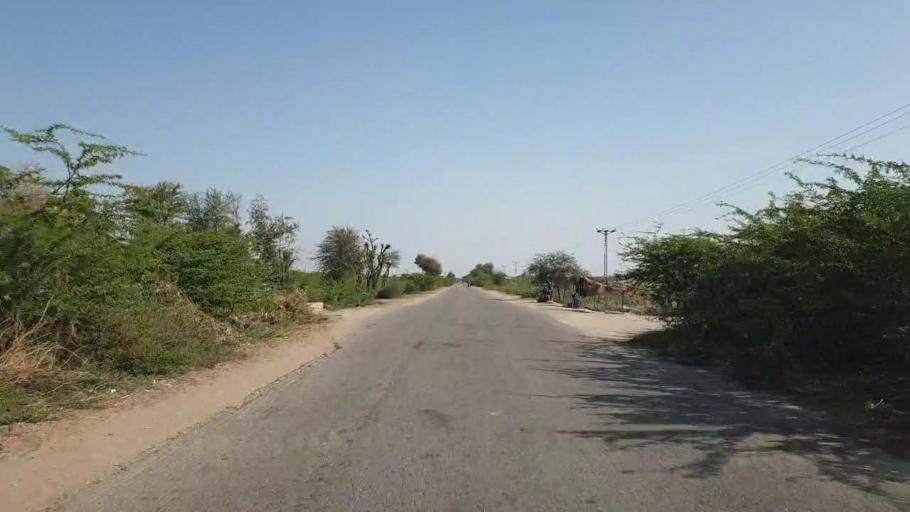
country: PK
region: Sindh
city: Chor
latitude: 25.4781
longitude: 69.7753
